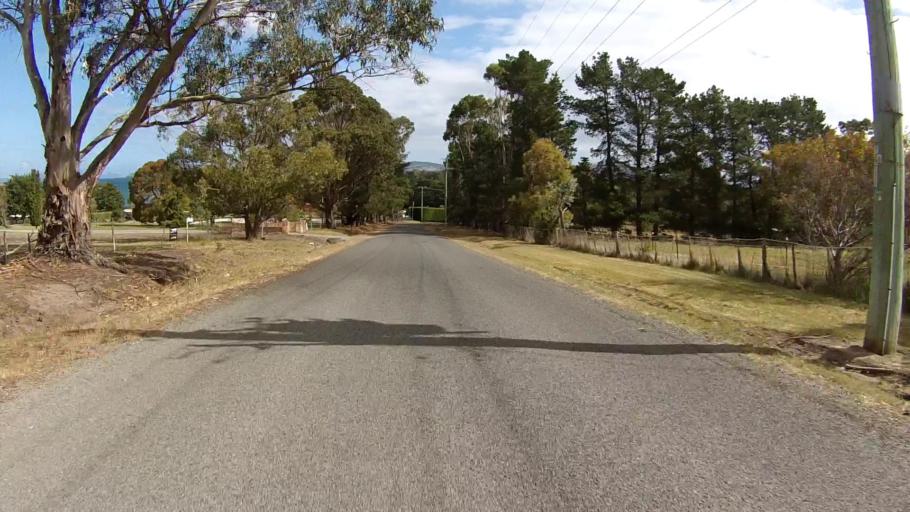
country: AU
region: Tasmania
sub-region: Clarence
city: Acton Park
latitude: -42.8866
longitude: 147.5008
